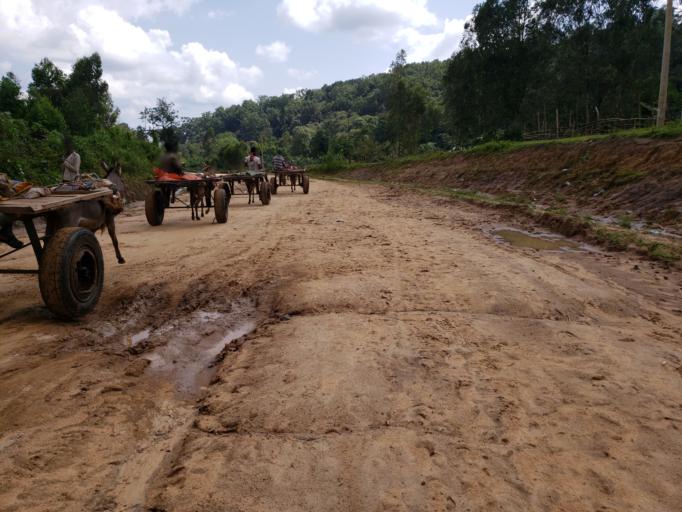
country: ET
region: Oromiya
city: Dodola
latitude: 6.4546
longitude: 39.5691
